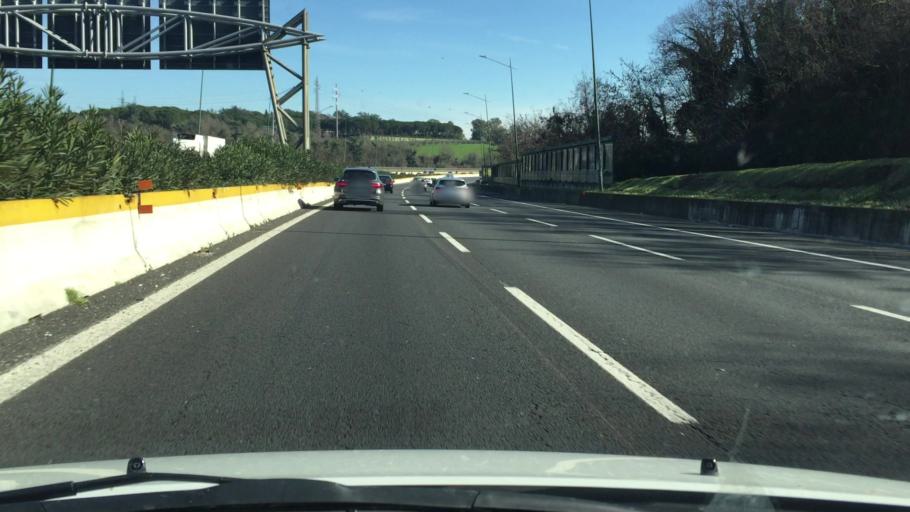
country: VA
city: Vatican City
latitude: 41.9818
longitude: 12.4416
